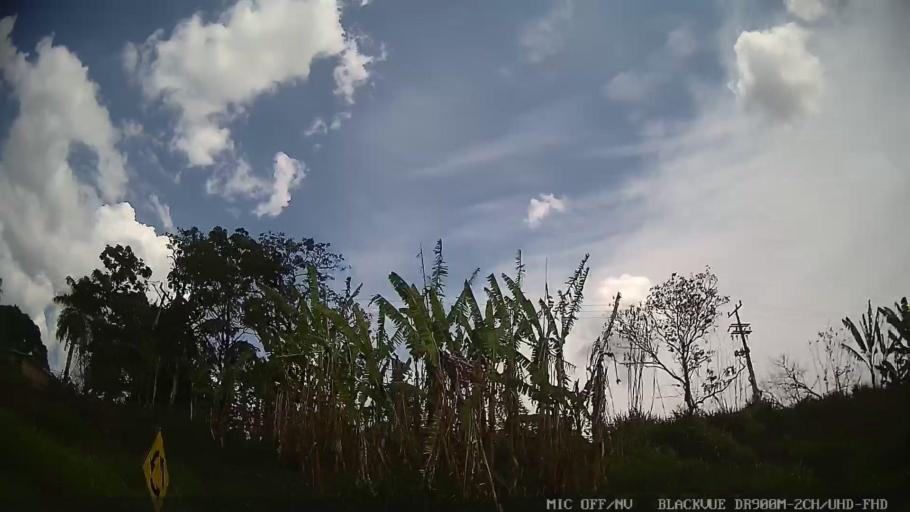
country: BR
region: Sao Paulo
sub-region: Itatiba
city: Itatiba
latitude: -22.9614
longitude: -46.7117
